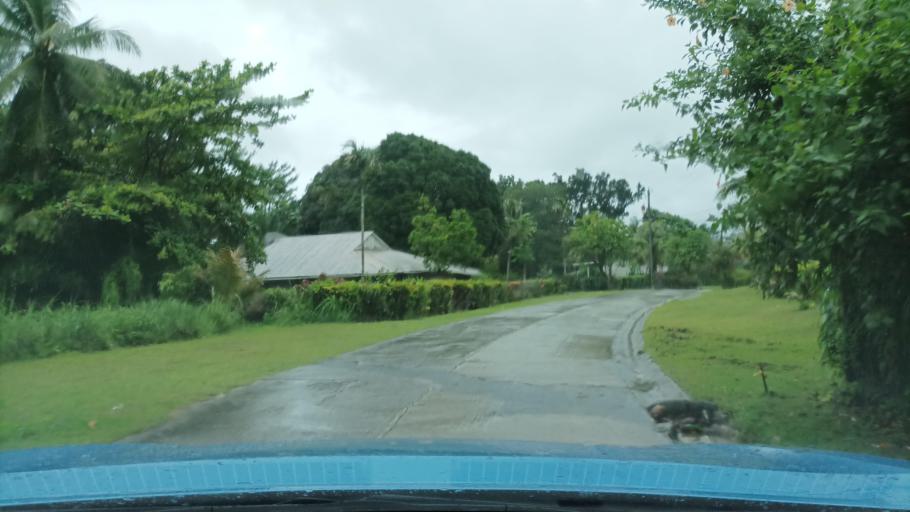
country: FM
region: Pohnpei
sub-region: Kolonia Municipality
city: Kolonia
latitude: 6.9579
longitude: 158.2134
